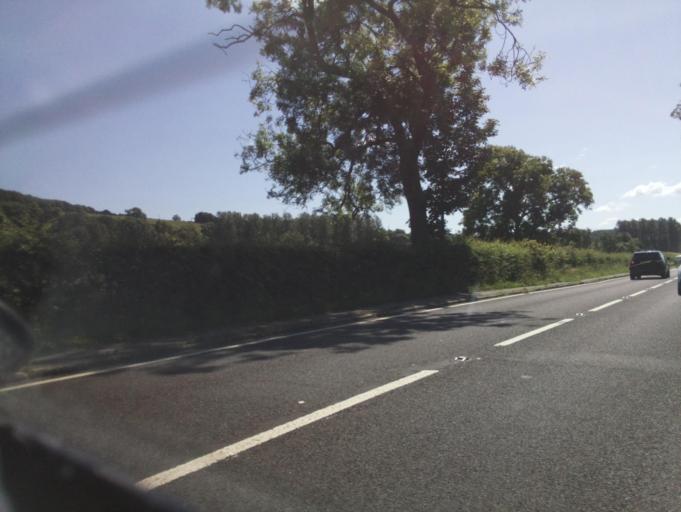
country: GB
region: England
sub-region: Derbyshire
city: Bakewell
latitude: 53.2030
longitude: -1.6643
